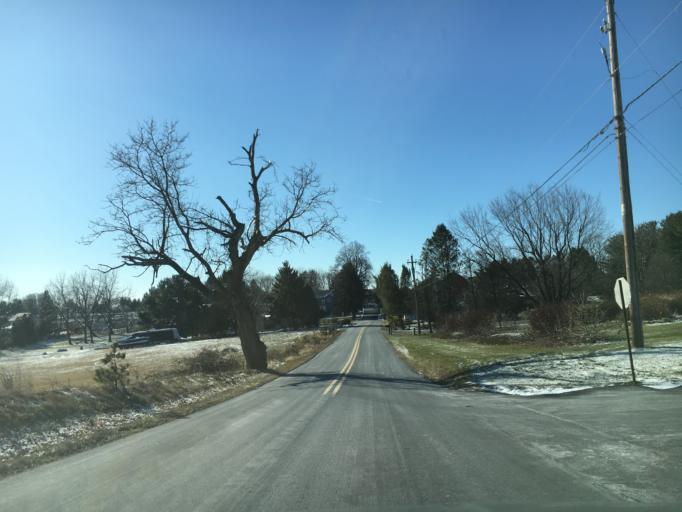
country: US
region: Pennsylvania
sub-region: Lehigh County
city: Egypt
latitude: 40.6840
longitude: -75.5689
